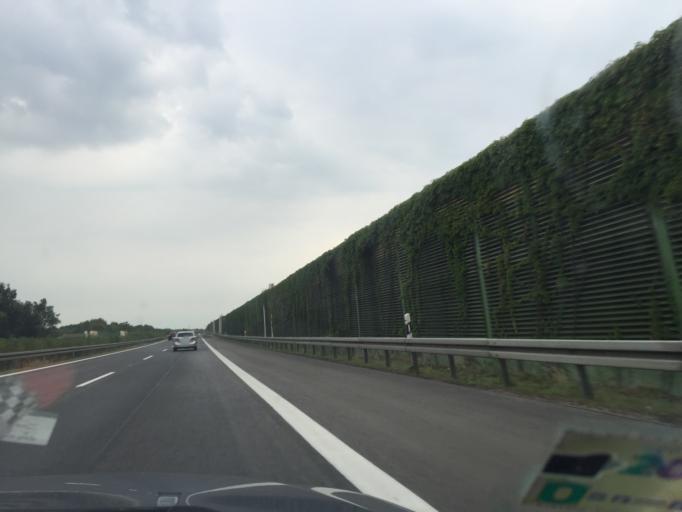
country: DE
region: Brandenburg
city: Bernau bei Berlin
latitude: 52.6751
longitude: 13.5655
